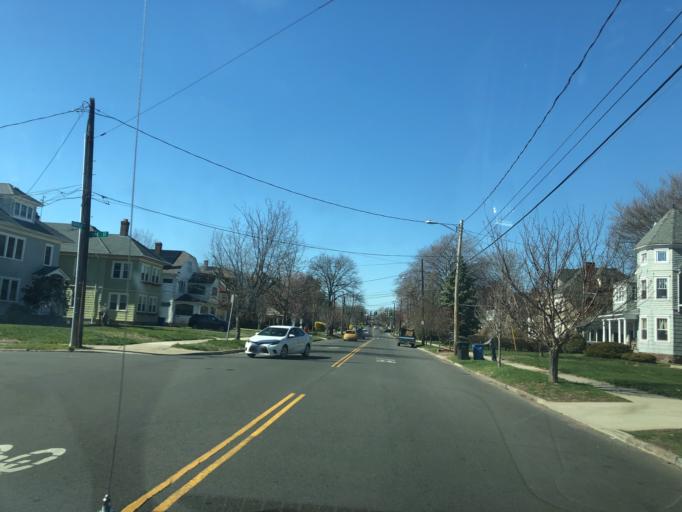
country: US
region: Connecticut
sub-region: Hartford County
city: Hartford
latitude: 41.7309
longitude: -72.6917
